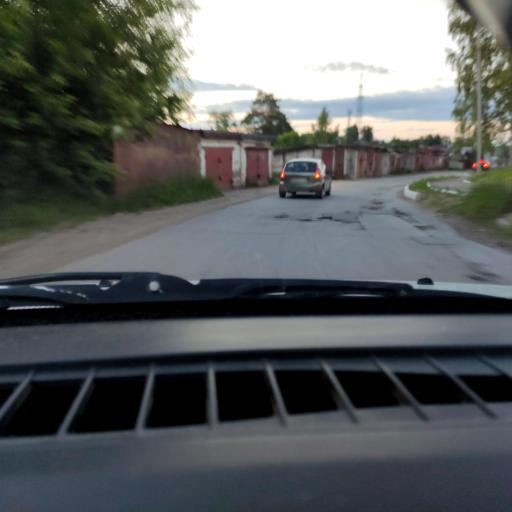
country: RU
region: Perm
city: Perm
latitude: 58.1153
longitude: 56.3096
